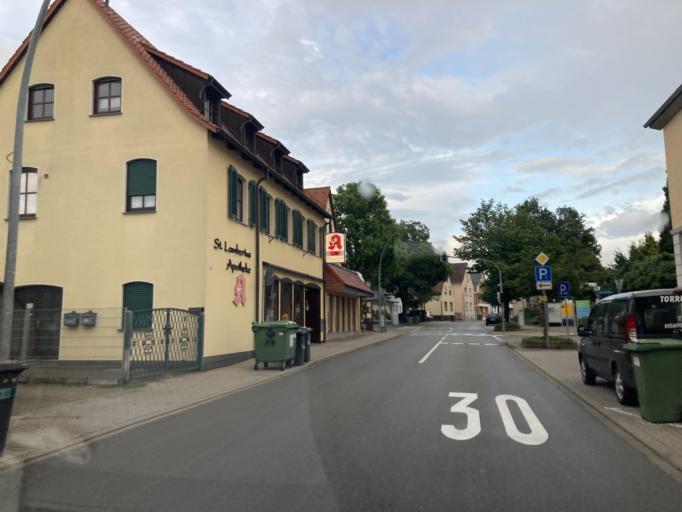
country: DE
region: Baden-Wuerttemberg
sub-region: Karlsruhe Region
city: Kronau
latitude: 49.2188
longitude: 8.6578
